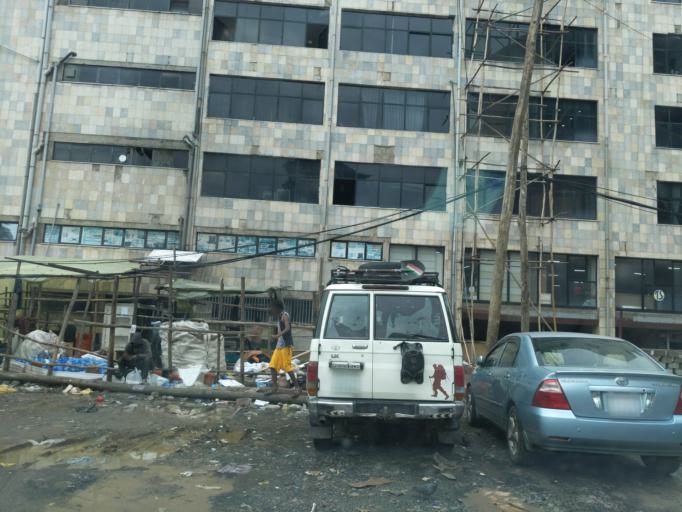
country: ET
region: Adis Abeba
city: Addis Ababa
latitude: 8.9964
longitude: 38.7868
